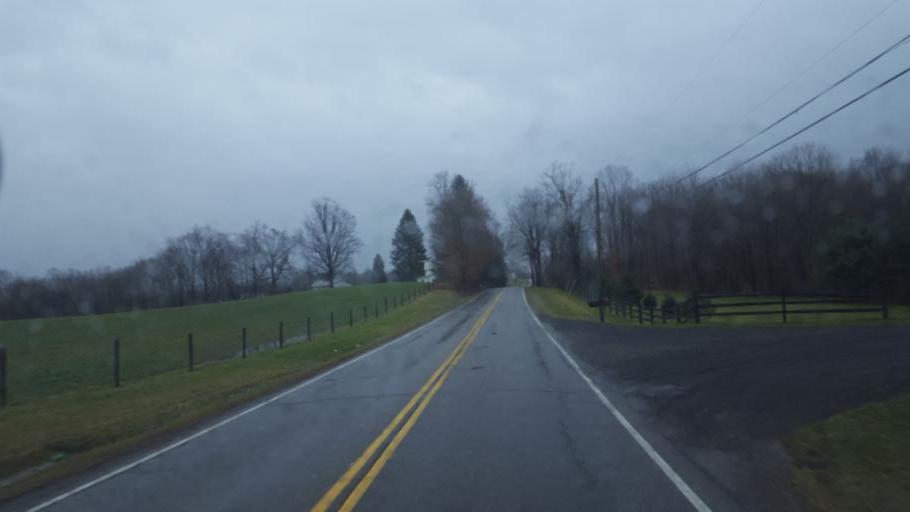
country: US
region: Ohio
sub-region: Geauga County
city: Middlefield
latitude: 41.3836
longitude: -81.0031
